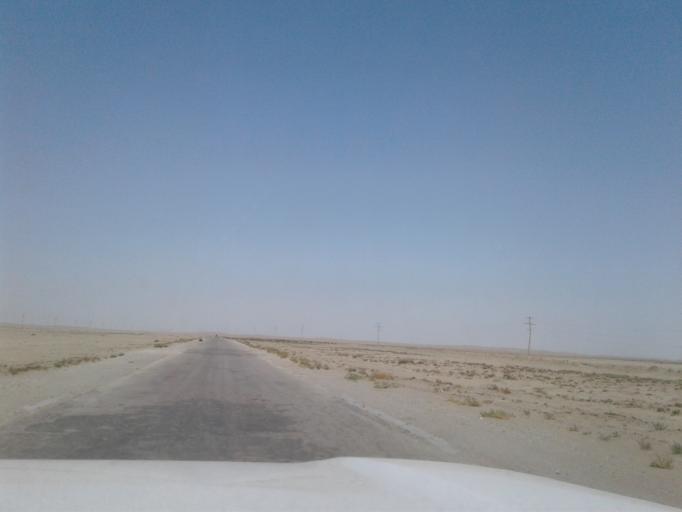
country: TM
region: Balkan
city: Gumdag
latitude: 38.3501
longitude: 54.3696
